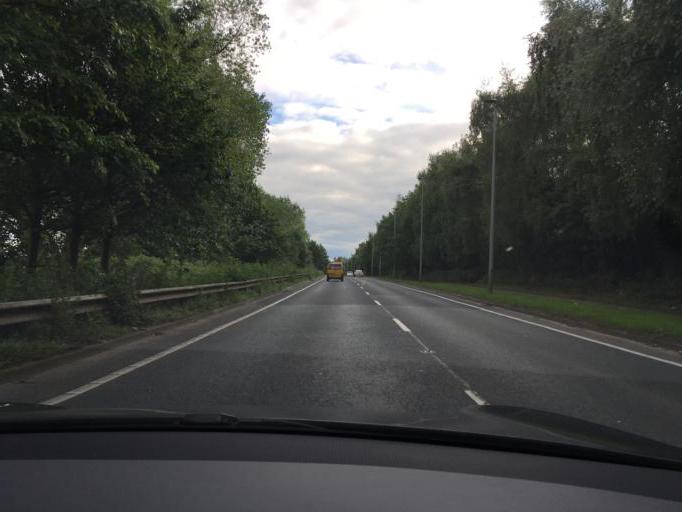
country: GB
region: England
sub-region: City and Borough of Salford
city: Irlam
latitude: 53.4511
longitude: -2.4064
